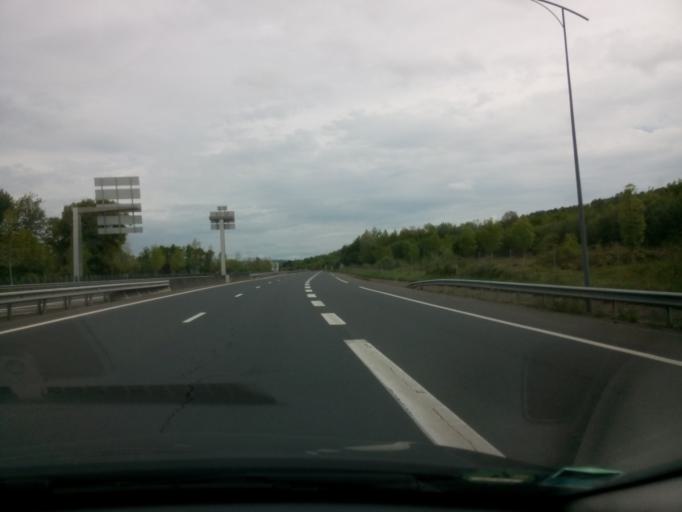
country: FR
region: Limousin
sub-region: Departement de la Correze
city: Varetz
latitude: 45.1720
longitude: 1.4683
